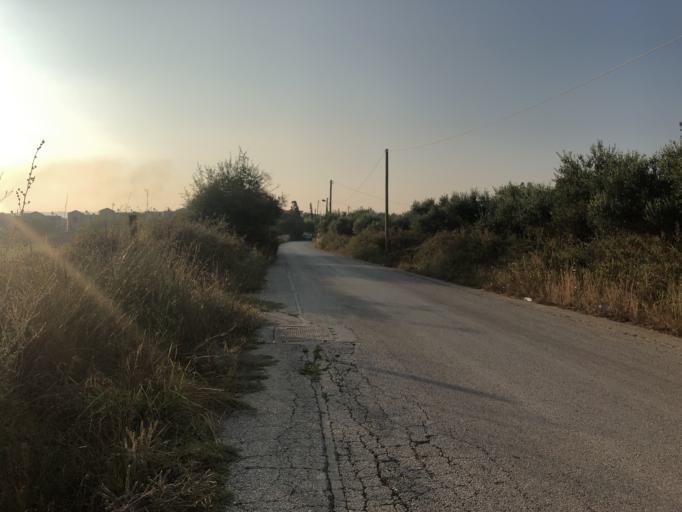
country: GR
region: Crete
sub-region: Nomos Chanias
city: Georgioupolis
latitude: 35.3496
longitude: 24.2827
